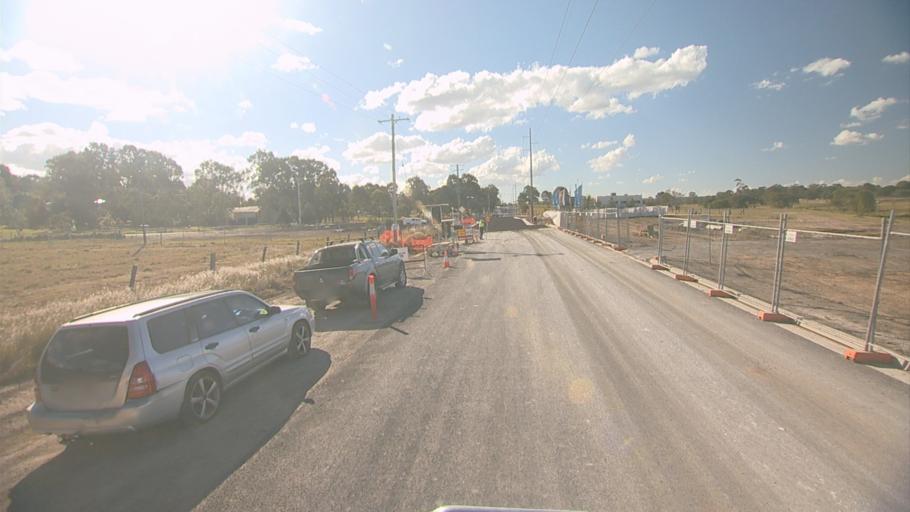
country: AU
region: Queensland
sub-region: Logan
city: Logan Reserve
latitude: -27.7183
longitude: 153.1150
